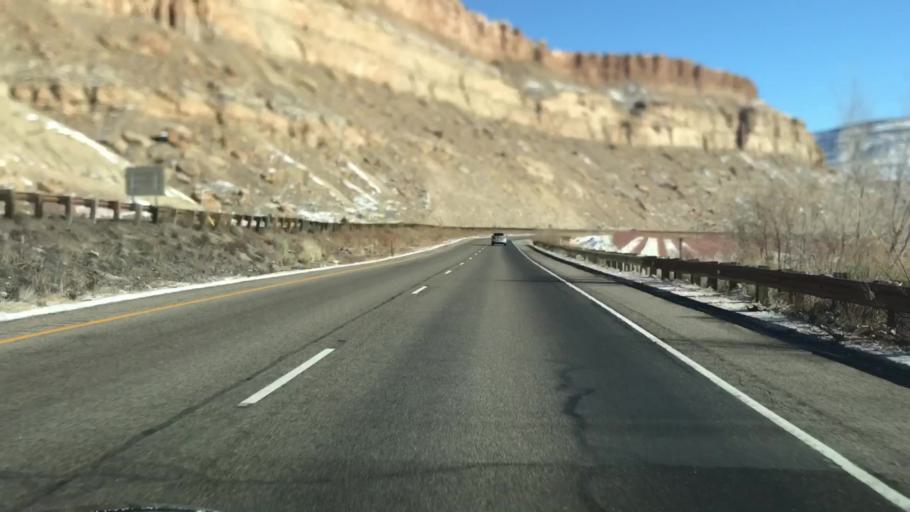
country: US
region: Colorado
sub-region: Mesa County
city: Palisade
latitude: 39.1184
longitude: -108.3427
